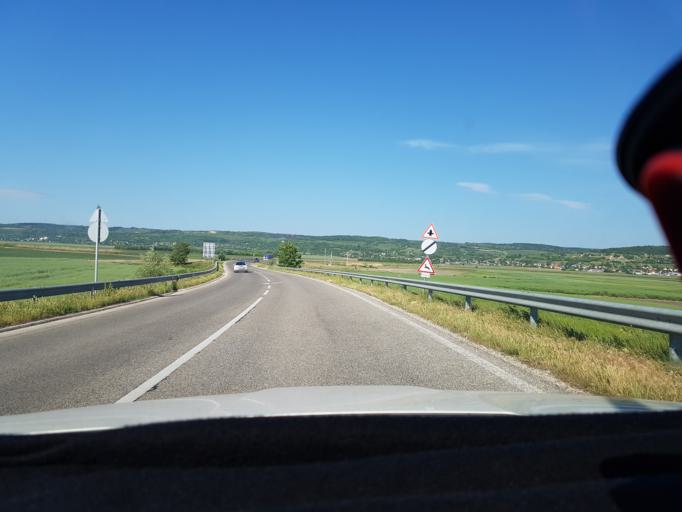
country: HU
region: Tolna
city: Ocseny
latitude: 46.3087
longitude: 18.7206
